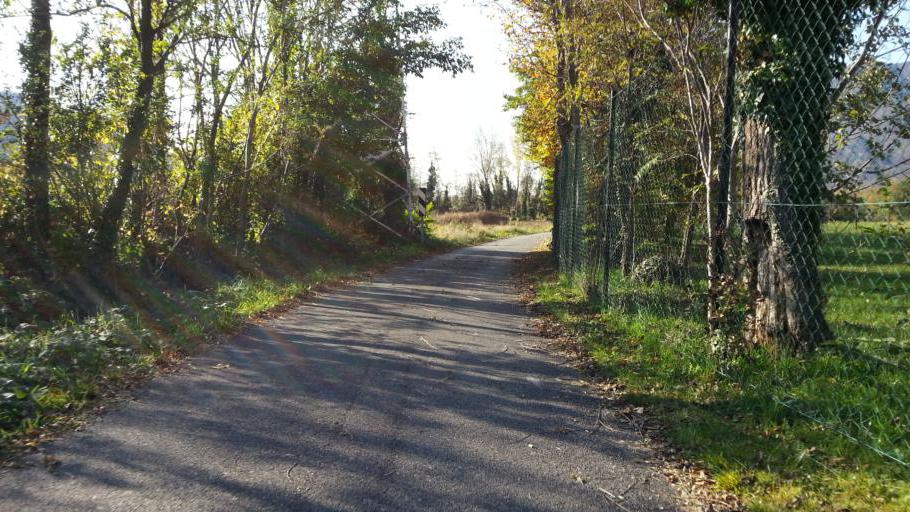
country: IT
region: Friuli Venezia Giulia
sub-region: Provincia di Udine
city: Venzone
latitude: 46.3271
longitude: 13.1312
